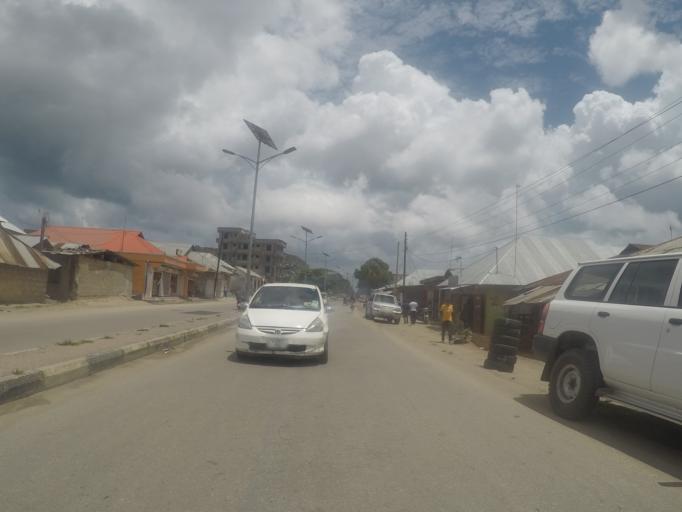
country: TZ
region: Zanzibar Urban/West
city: Zanzibar
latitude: -6.1713
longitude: 39.2153
